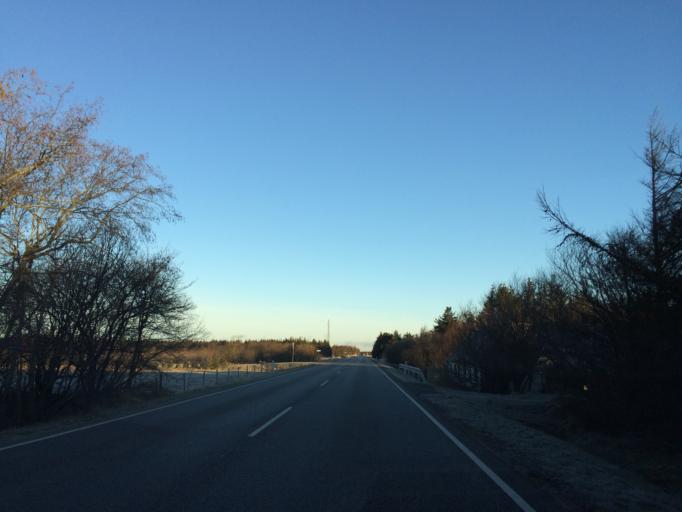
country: DK
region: Central Jutland
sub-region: Holstebro Kommune
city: Ulfborg
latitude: 56.3962
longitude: 8.3194
